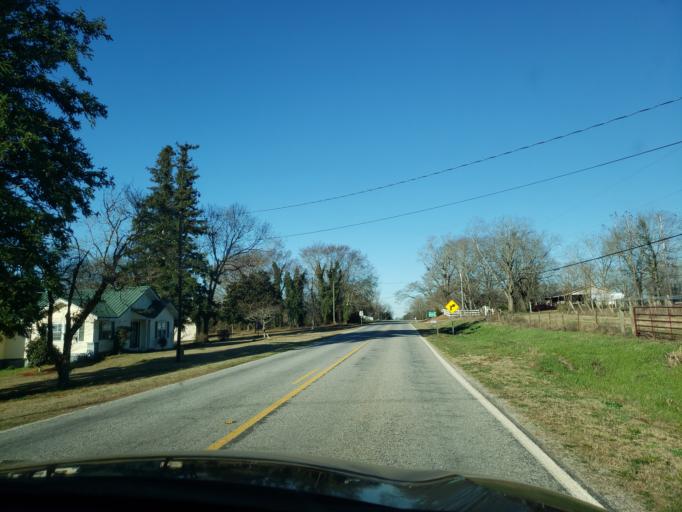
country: US
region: Alabama
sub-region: Elmore County
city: Tallassee
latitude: 32.5812
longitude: -85.7857
